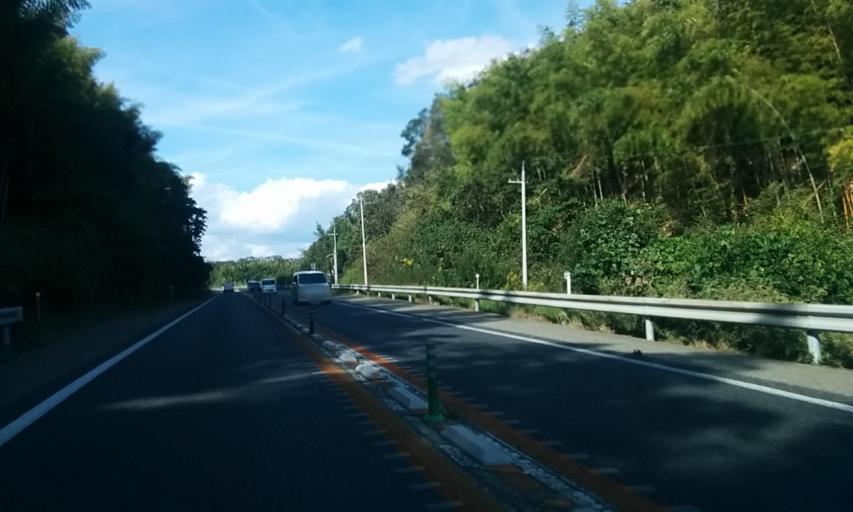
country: JP
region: Kyoto
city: Tanabe
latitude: 34.7605
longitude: 135.7779
